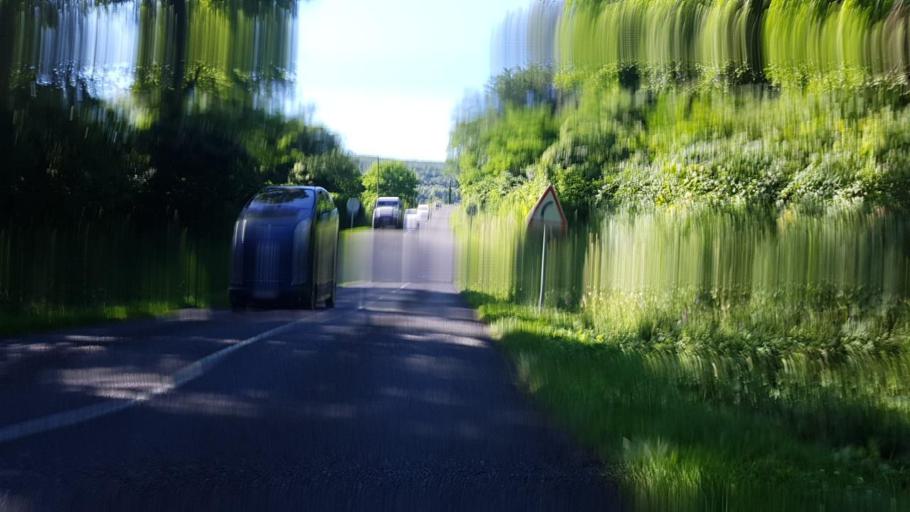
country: FR
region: Picardie
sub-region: Departement de l'Aisne
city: Chezy-sur-Marne
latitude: 48.9904
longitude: 3.3432
